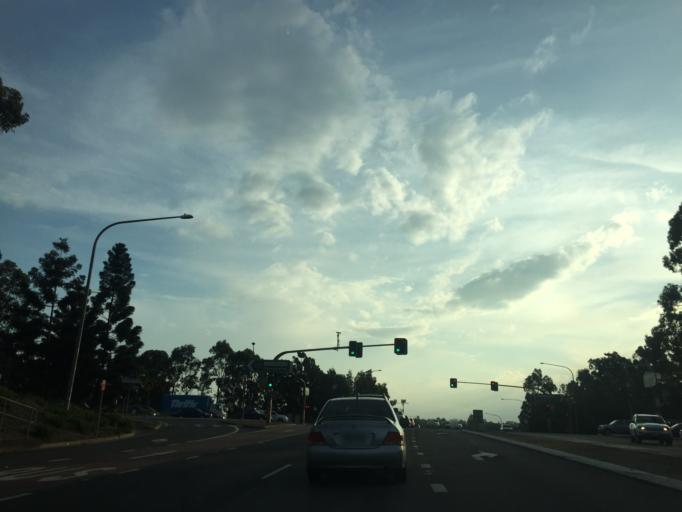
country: AU
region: New South Wales
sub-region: Blacktown
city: Stanhope Gardens
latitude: -33.7203
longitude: 150.9385
